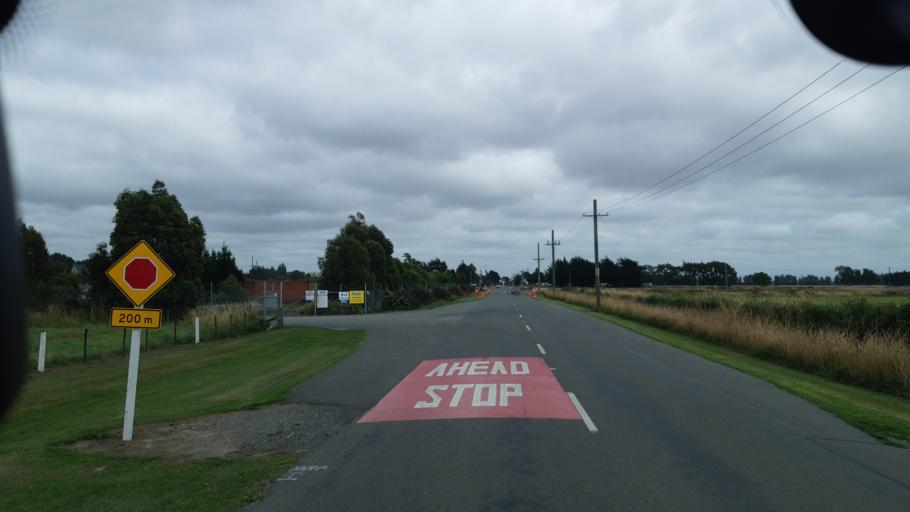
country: NZ
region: Canterbury
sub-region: Selwyn District
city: Prebbleton
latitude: -43.5057
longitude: 172.5163
